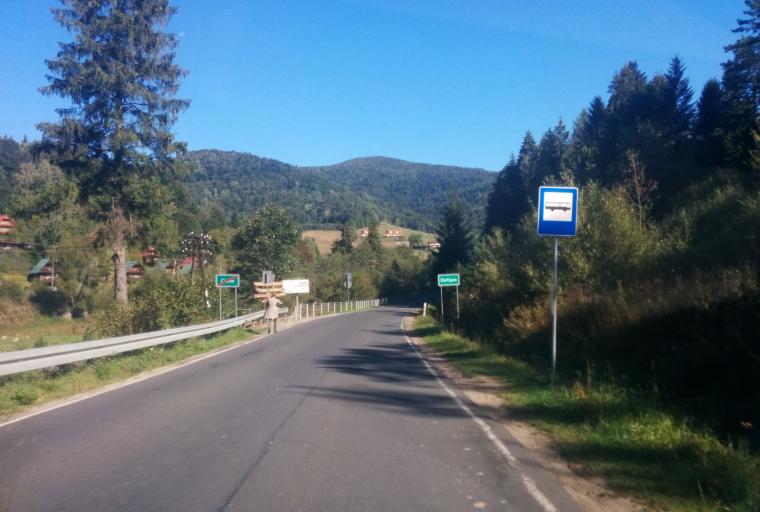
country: PL
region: Subcarpathian Voivodeship
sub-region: Powiat leski
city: Cisna
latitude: 49.2180
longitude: 22.3348
